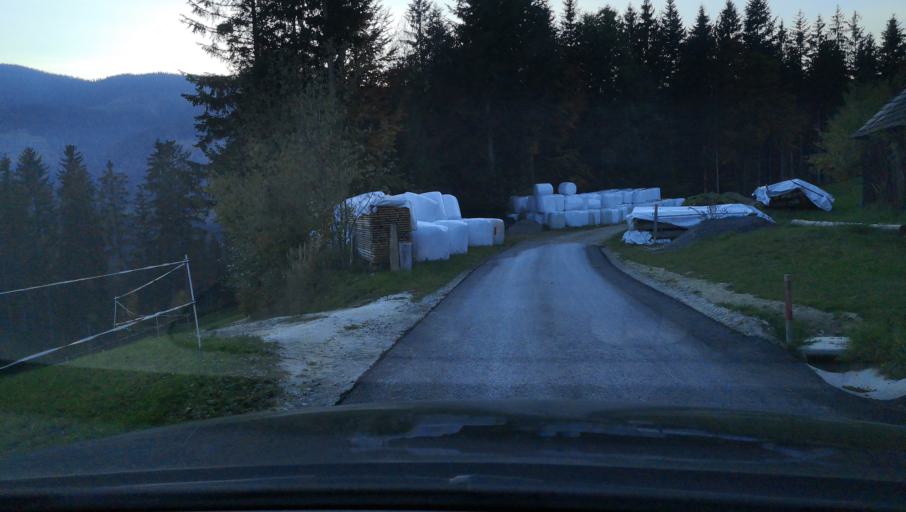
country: AT
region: Styria
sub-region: Politischer Bezirk Weiz
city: Birkfeld
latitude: 47.3587
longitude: 15.6715
